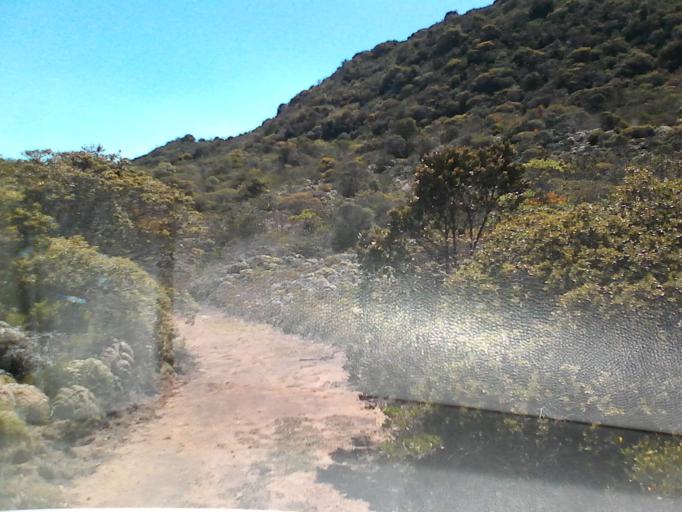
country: CO
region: Boyaca
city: Sachica
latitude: 5.5295
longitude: -73.5456
